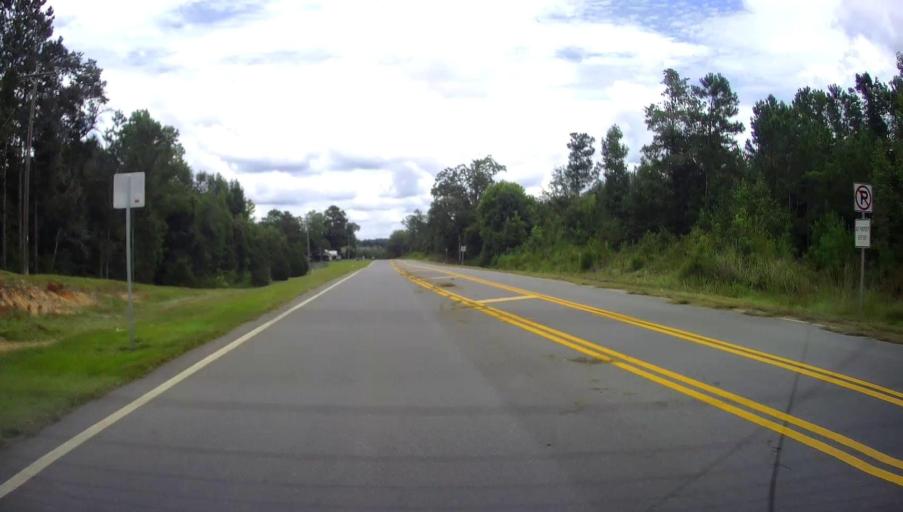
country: US
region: Georgia
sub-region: Schley County
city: Ellaville
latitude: 32.2623
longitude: -84.2040
